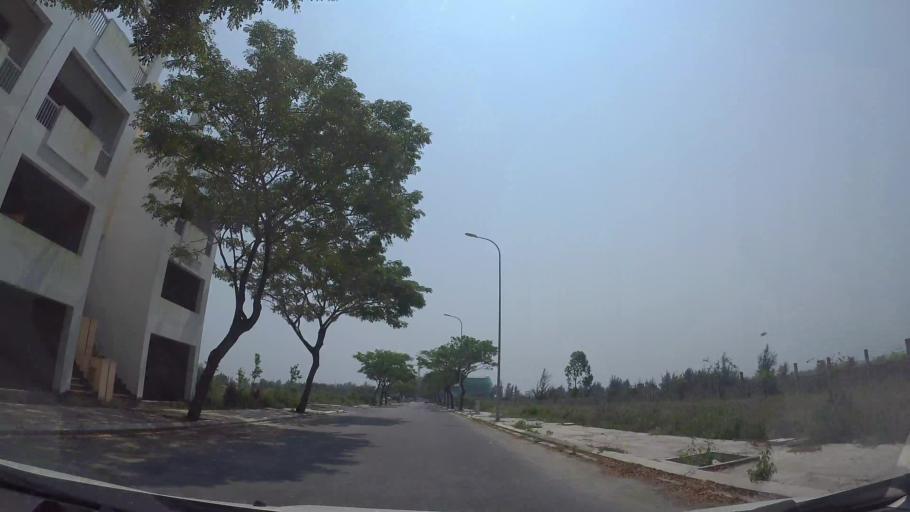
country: VN
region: Da Nang
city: Ngu Hanh Son
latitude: 15.9712
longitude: 108.2610
